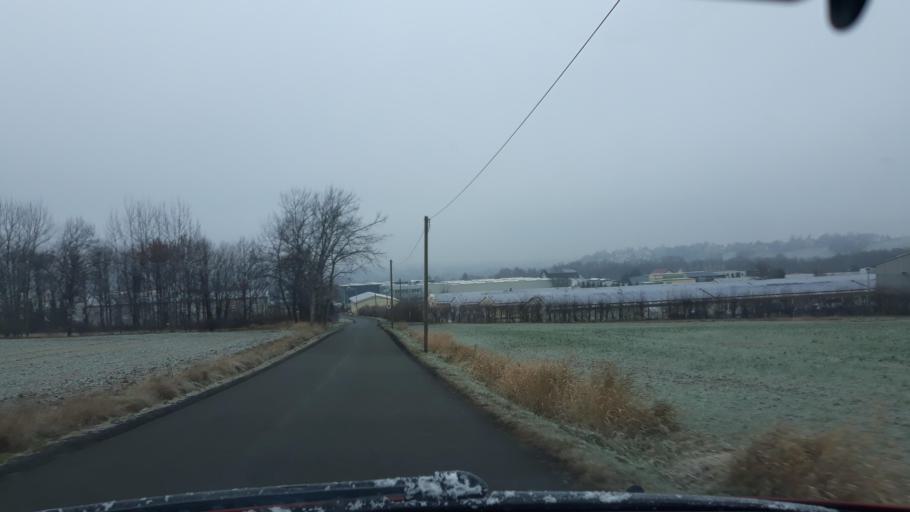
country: DE
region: Saxony
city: Wilkau-Hasslau
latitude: 50.6853
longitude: 12.5205
